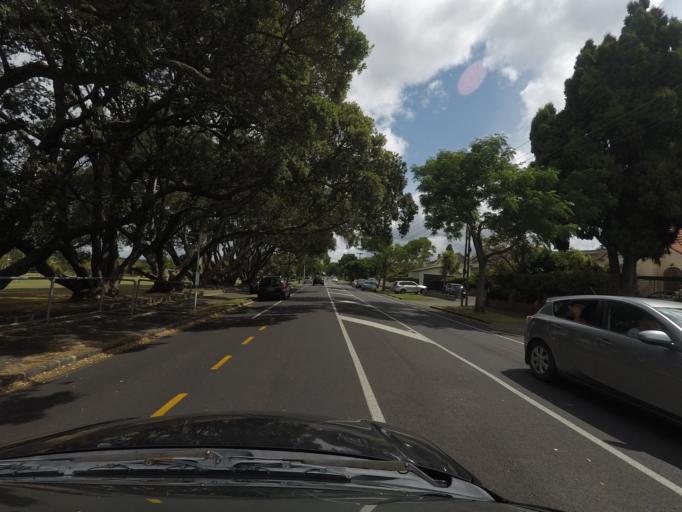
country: NZ
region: Auckland
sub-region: Auckland
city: Auckland
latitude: -36.8949
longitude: 174.7227
